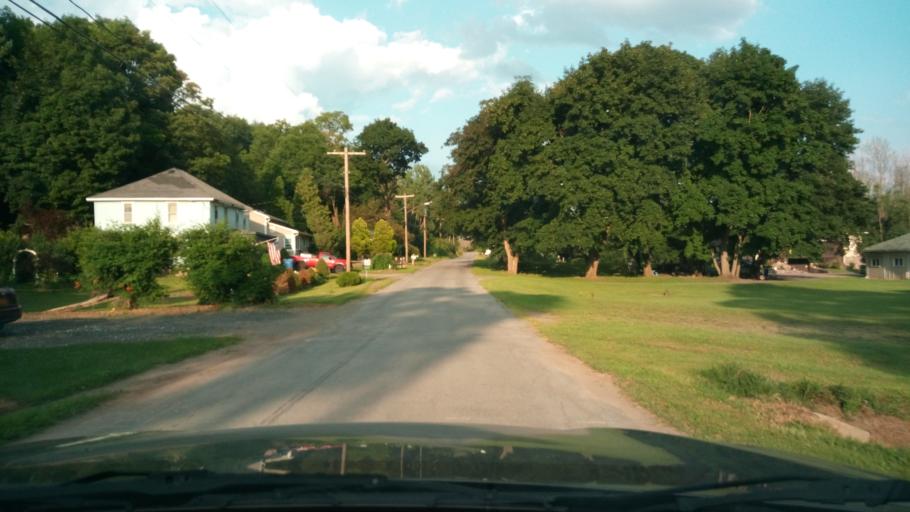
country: US
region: New York
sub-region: Wayne County
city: Lyons
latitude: 43.0787
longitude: -76.9443
